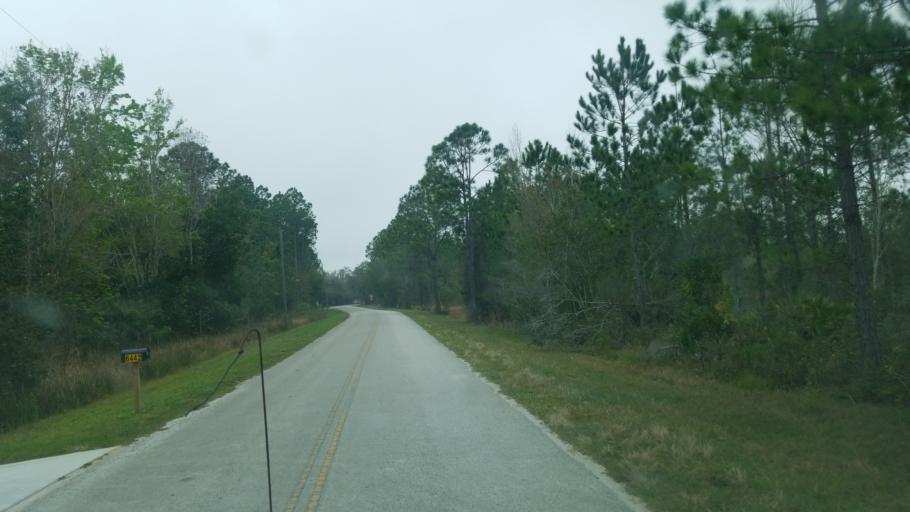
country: US
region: Florida
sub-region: Lake County
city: Groveland
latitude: 28.3830
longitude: -81.8473
